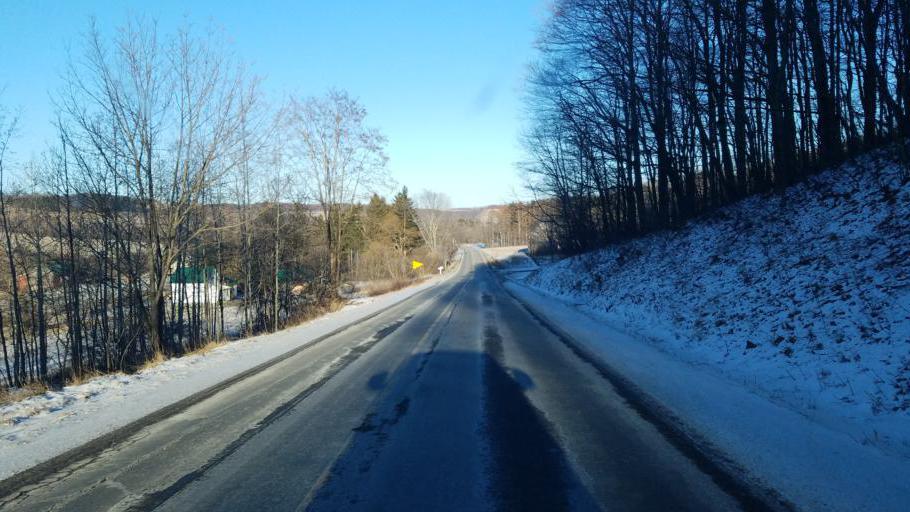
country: US
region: Pennsylvania
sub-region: Tioga County
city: Westfield
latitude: 41.9410
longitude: -77.7085
